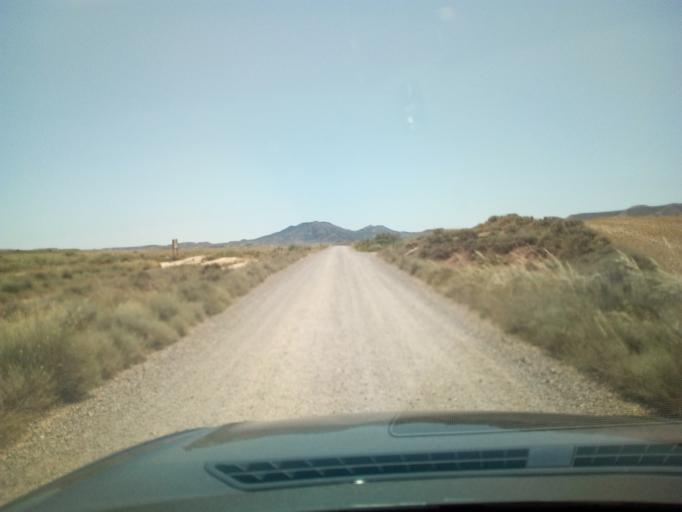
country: ES
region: Navarre
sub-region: Provincia de Navarra
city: Arguedas
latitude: 42.1806
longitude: -1.4575
